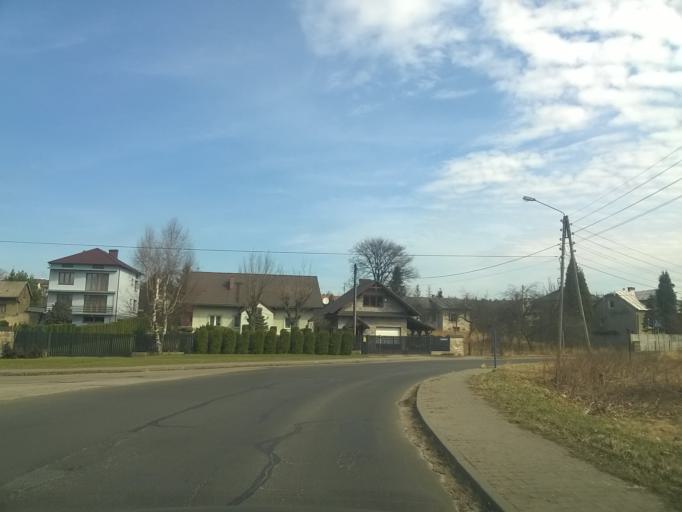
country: PL
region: Lesser Poland Voivodeship
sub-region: Powiat chrzanowski
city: Luszowice
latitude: 50.1958
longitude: 19.4323
